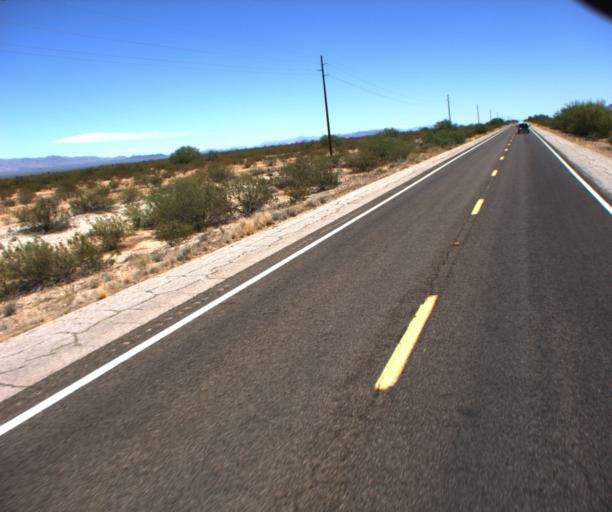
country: US
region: Arizona
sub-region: La Paz County
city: Salome
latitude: 33.8570
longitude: -113.4314
